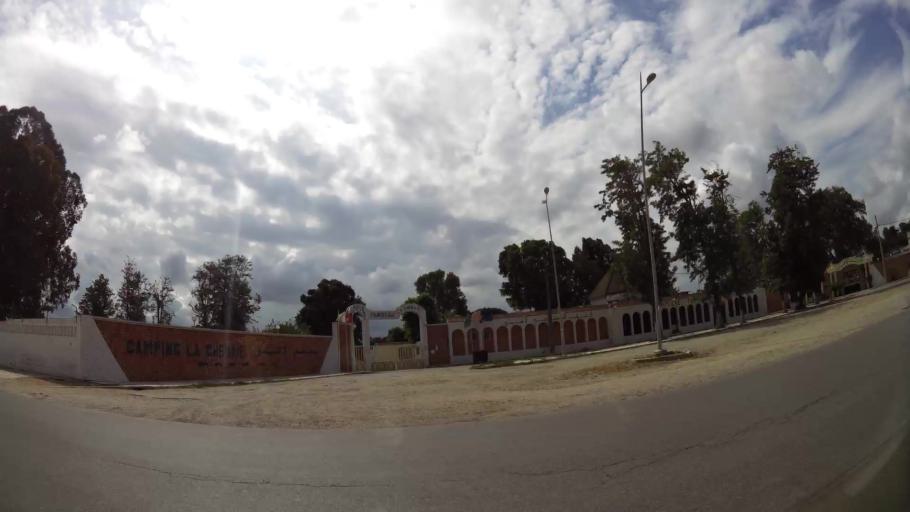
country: MA
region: Gharb-Chrarda-Beni Hssen
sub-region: Kenitra Province
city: Kenitra
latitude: 34.2568
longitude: -6.5681
